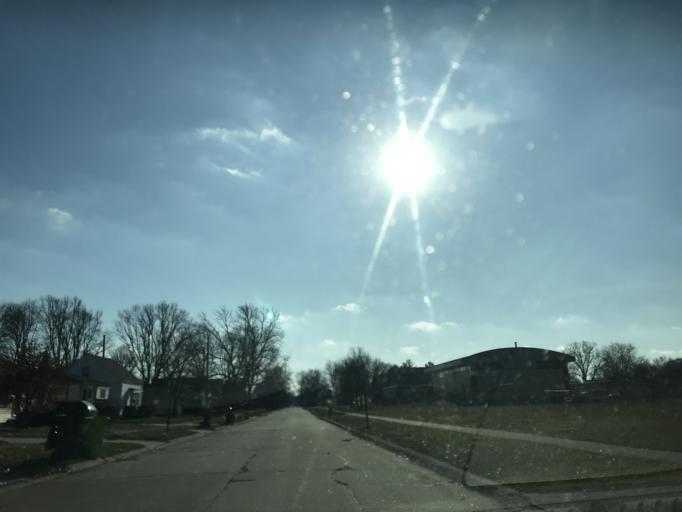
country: US
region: Michigan
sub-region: Oakland County
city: Madison Heights
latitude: 42.4954
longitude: -83.1137
